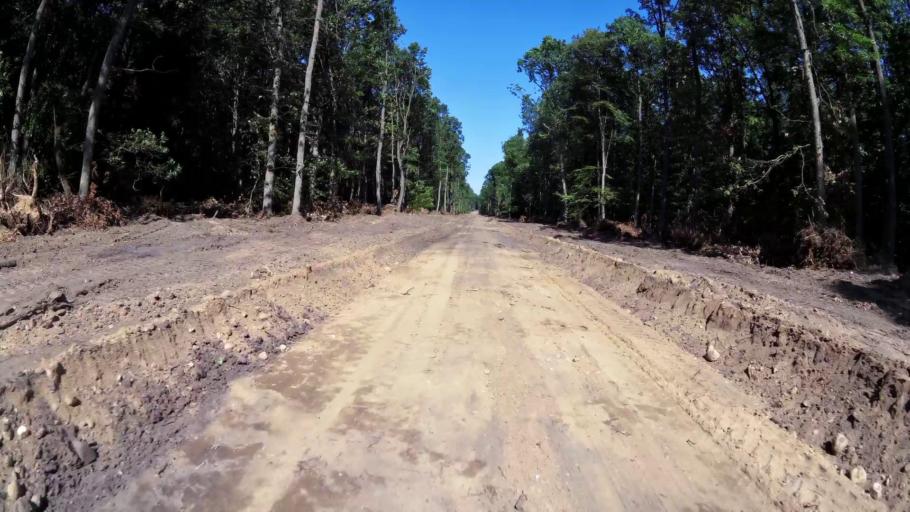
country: PL
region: West Pomeranian Voivodeship
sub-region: Powiat drawski
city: Wierzchowo
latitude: 53.3998
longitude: 16.2404
